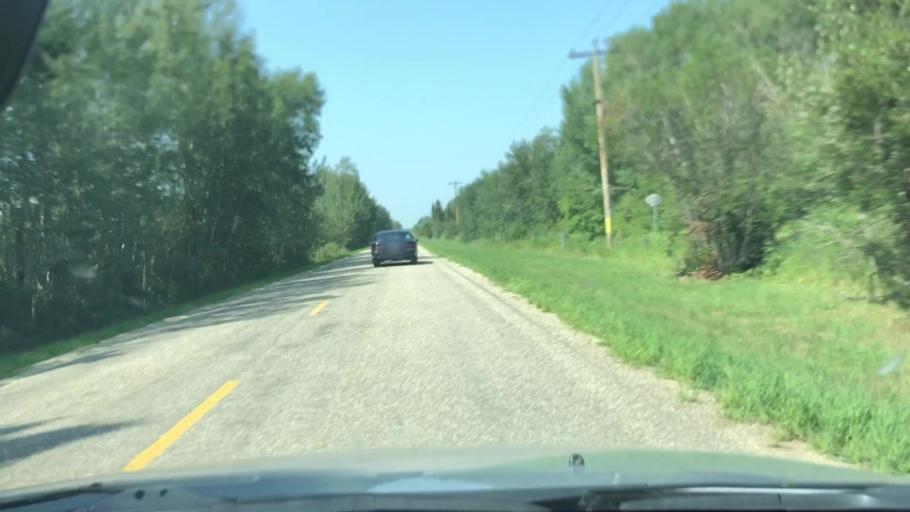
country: CA
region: Alberta
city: Devon
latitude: 53.4253
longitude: -113.7928
